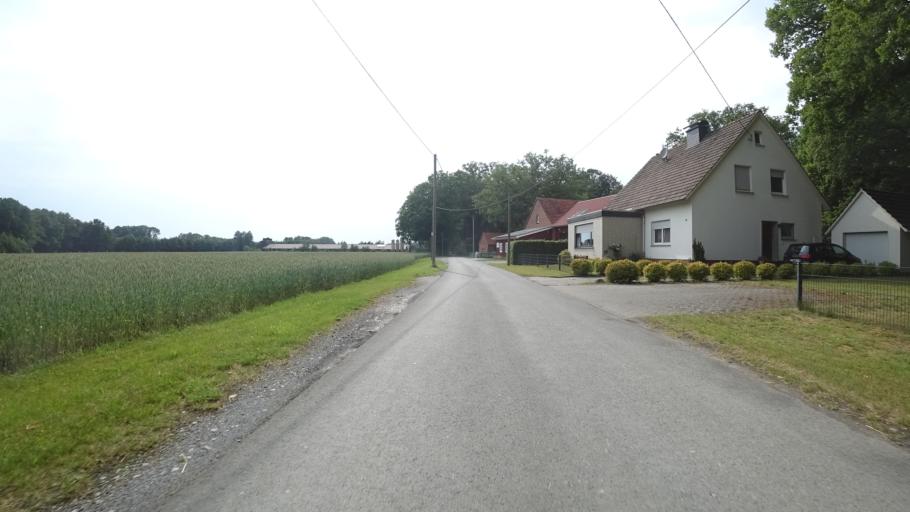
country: DE
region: North Rhine-Westphalia
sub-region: Regierungsbezirk Detmold
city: Guetersloh
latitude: 51.9493
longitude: 8.3659
